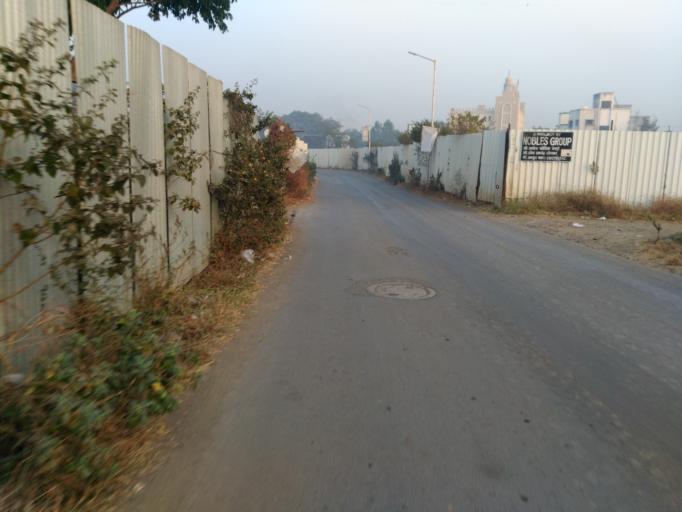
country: IN
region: Maharashtra
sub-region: Pune Division
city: Pune
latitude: 18.4431
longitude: 73.8862
